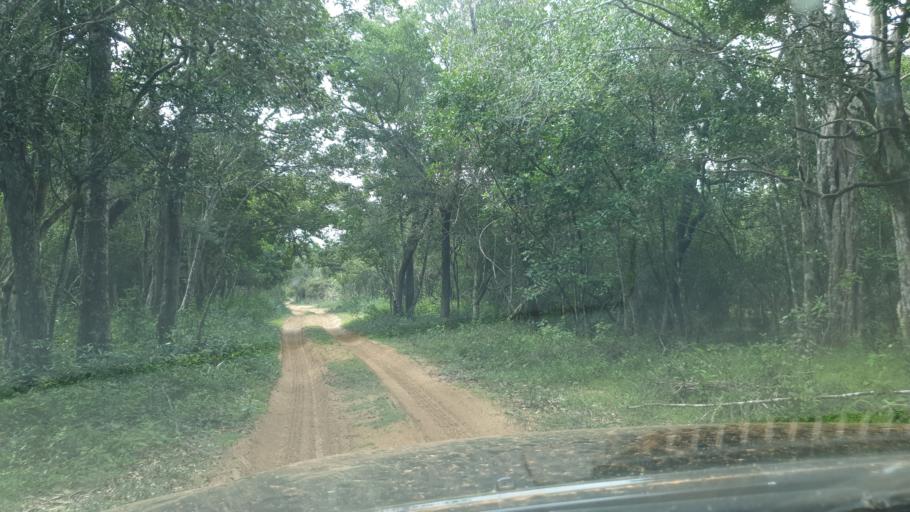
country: LK
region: North Western
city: Puttalam
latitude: 8.4184
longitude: 80.0052
